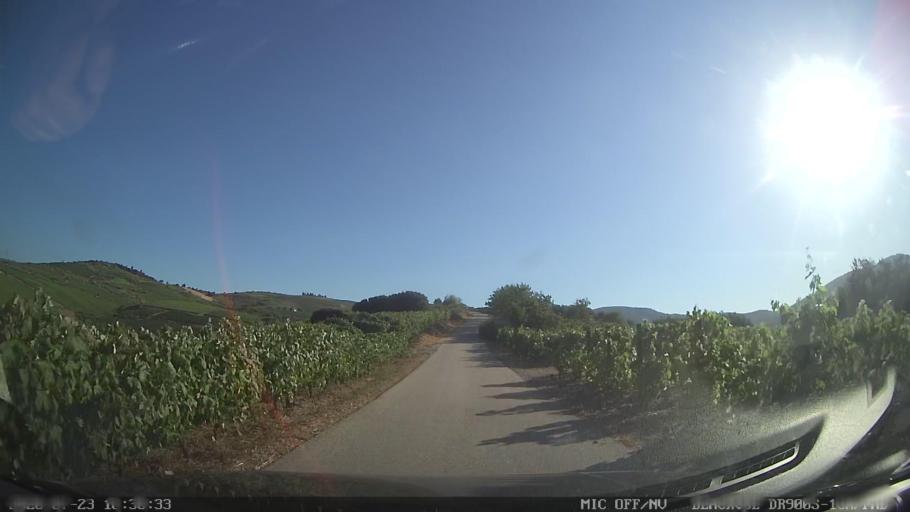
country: PT
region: Viseu
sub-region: Sao Joao da Pesqueira
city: Sao Joao da Pesqueira
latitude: 41.1792
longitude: -7.4041
